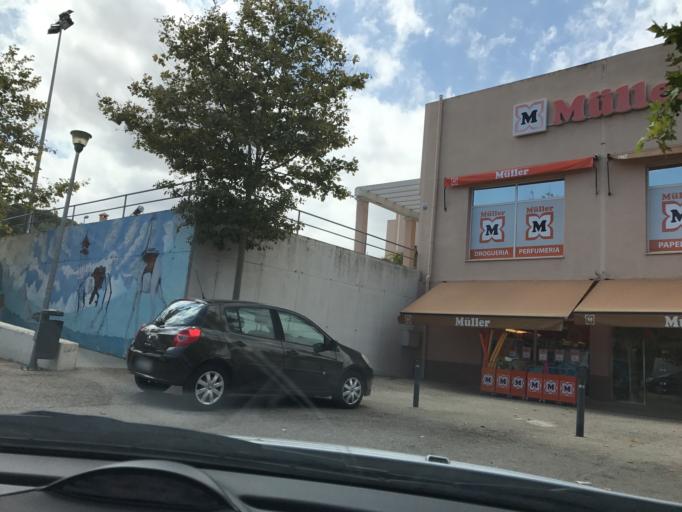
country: ES
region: Balearic Islands
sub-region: Illes Balears
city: Son Servera
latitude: 39.6177
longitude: 3.3639
